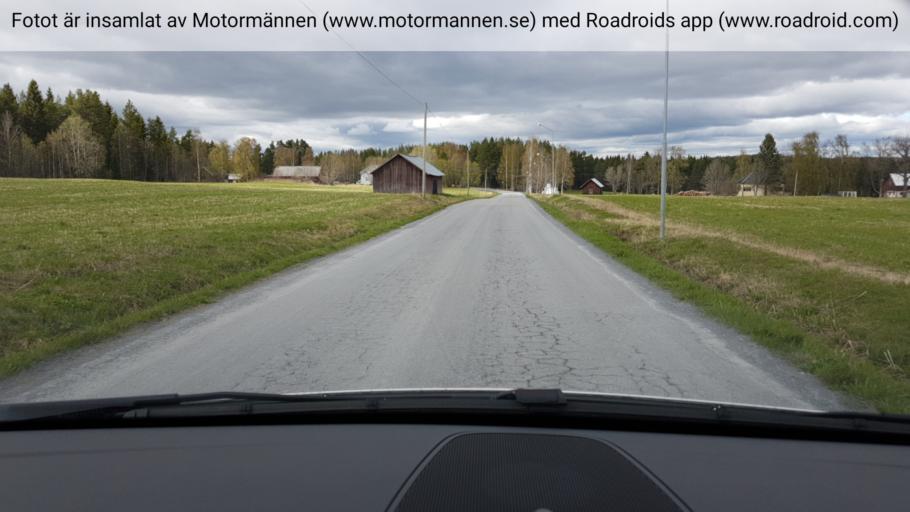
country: SE
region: Jaemtland
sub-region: OEstersunds Kommun
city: Lit
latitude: 63.2535
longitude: 14.8596
